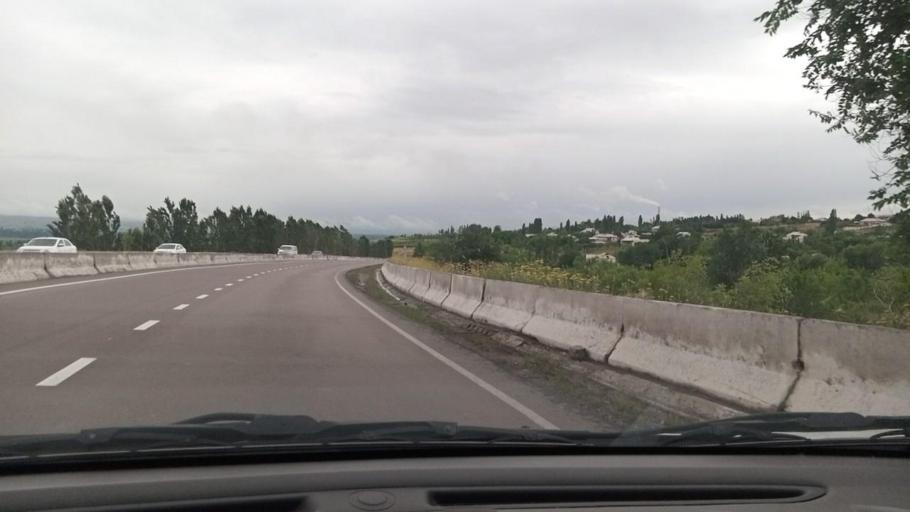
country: UZ
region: Toshkent
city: Angren
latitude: 40.9420
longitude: 69.9060
